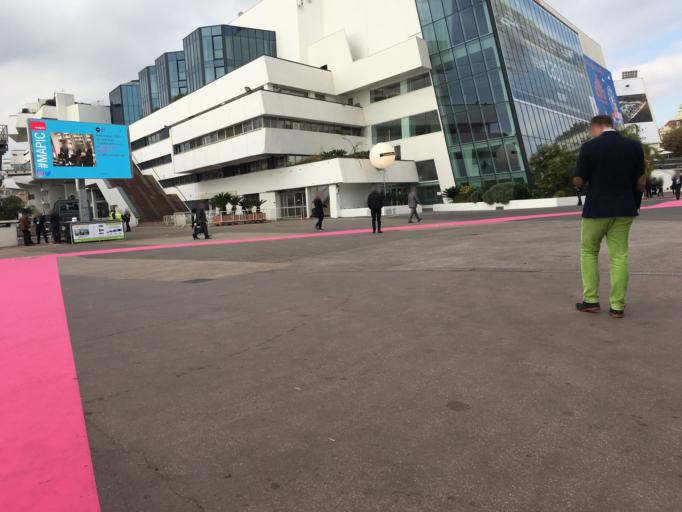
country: FR
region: Provence-Alpes-Cote d'Azur
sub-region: Departement des Alpes-Maritimes
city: Cannes
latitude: 43.5502
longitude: 7.0190
